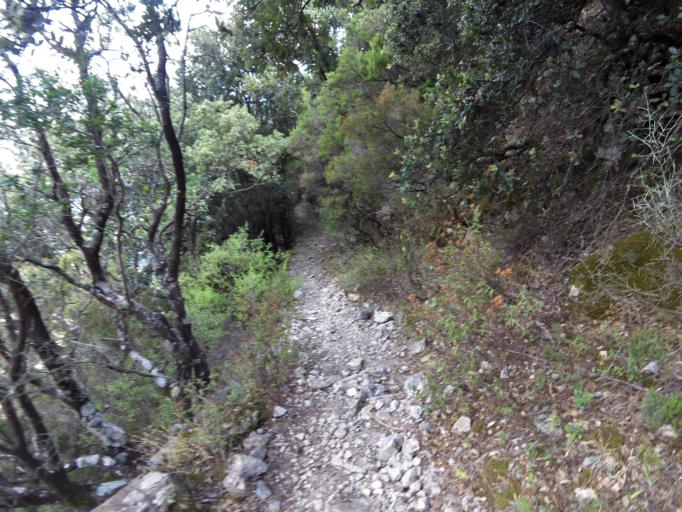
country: IT
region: Calabria
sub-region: Provincia di Reggio Calabria
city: Bivongi
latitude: 38.5003
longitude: 16.4003
